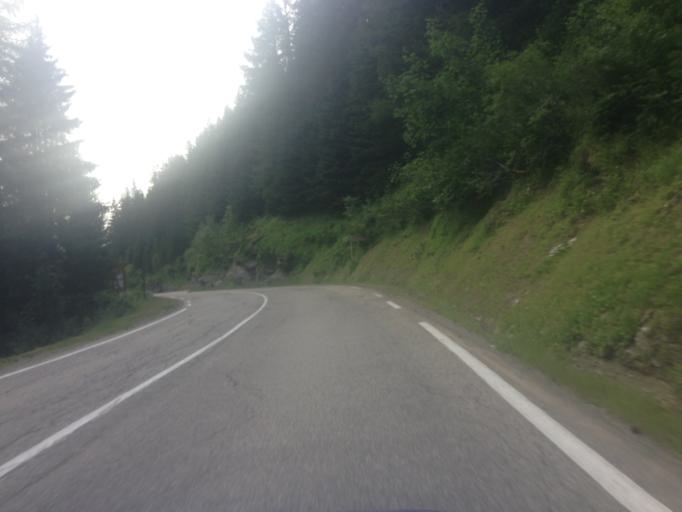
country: FR
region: Rhone-Alpes
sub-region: Departement de la Savoie
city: Tignes
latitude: 45.5217
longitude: 6.9141
